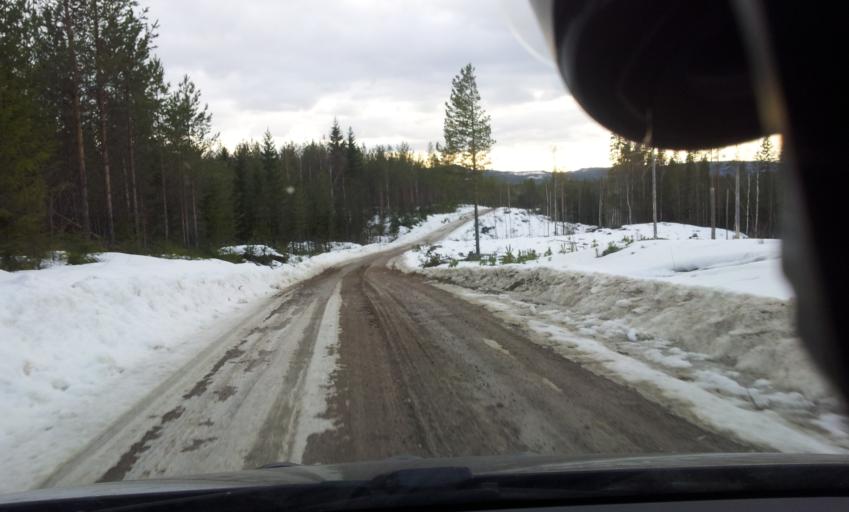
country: SE
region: Vaesternorrland
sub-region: Ange Kommun
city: Ange
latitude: 62.1910
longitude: 15.6870
